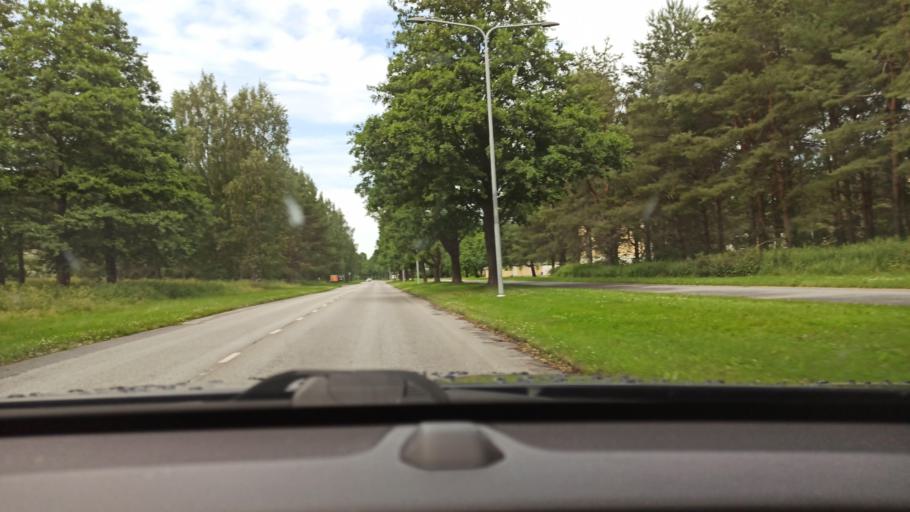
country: FI
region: Satakunta
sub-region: Pori
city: Pori
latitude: 61.5007
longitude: 21.7839
